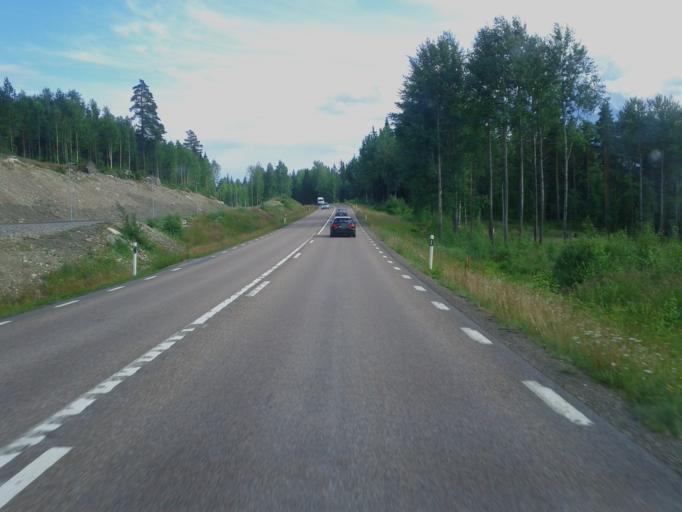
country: SE
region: Dalarna
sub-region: Faluns Kommun
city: Grycksbo
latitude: 60.6758
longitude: 15.5105
